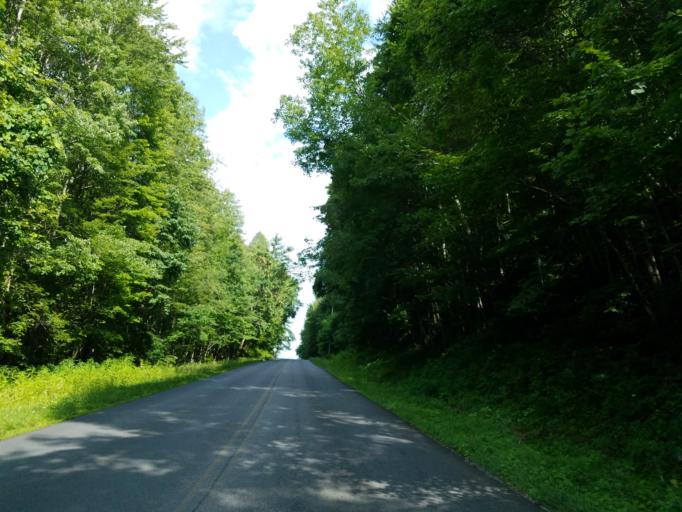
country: US
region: Georgia
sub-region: Fannin County
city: Blue Ridge
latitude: 34.8189
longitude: -84.3040
